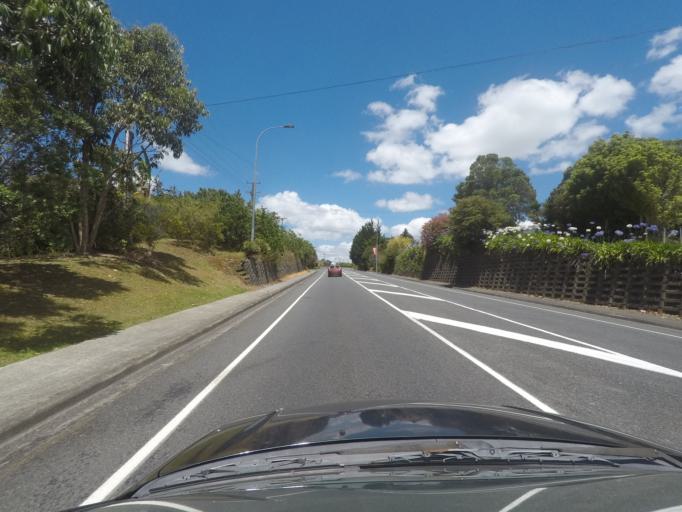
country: NZ
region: Northland
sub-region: Whangarei
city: Whangarei
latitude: -35.7447
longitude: 174.3665
